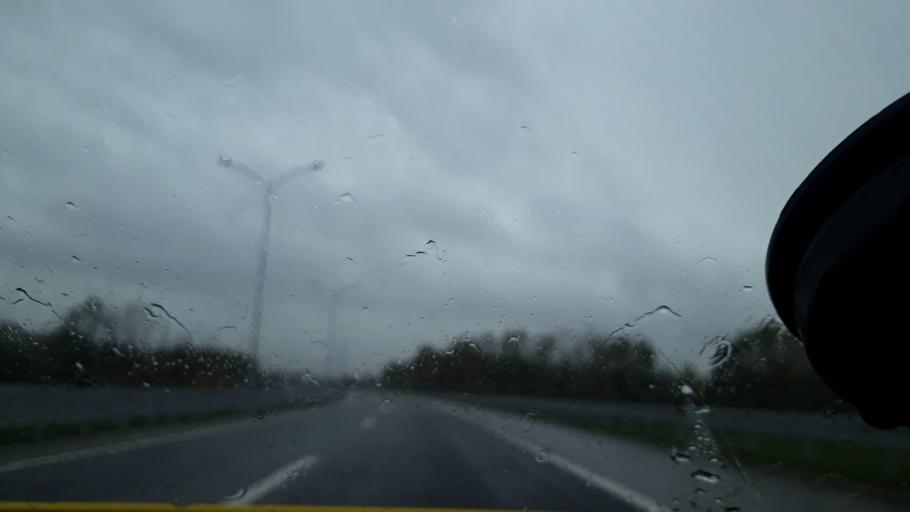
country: BA
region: Republika Srpska
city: Maglajani
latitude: 44.8963
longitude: 17.3628
